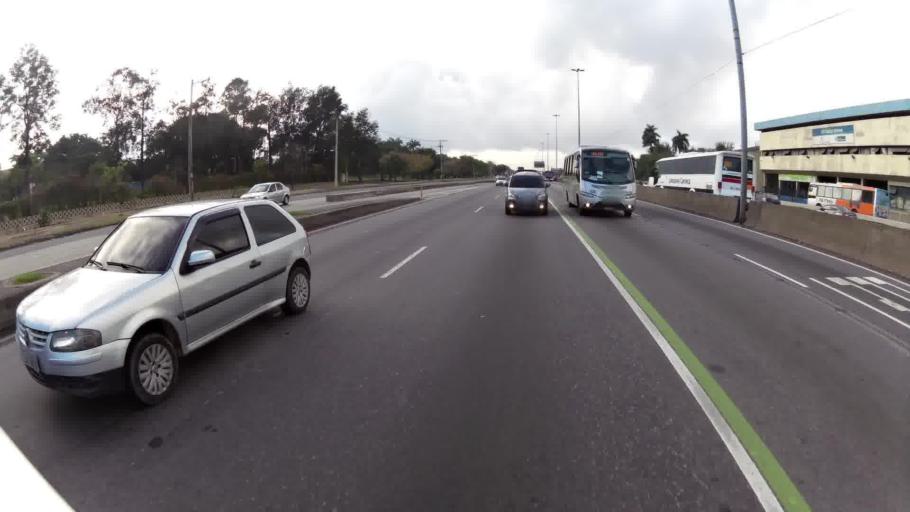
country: BR
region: Rio de Janeiro
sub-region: Duque De Caxias
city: Duque de Caxias
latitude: -22.8312
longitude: -43.2685
